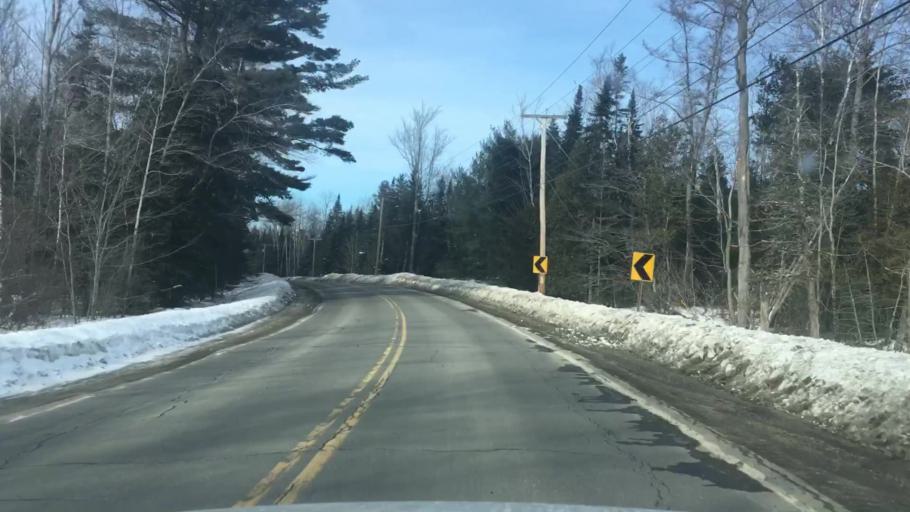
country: US
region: Maine
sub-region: Penobscot County
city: Charleston
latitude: 45.0457
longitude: -69.0290
